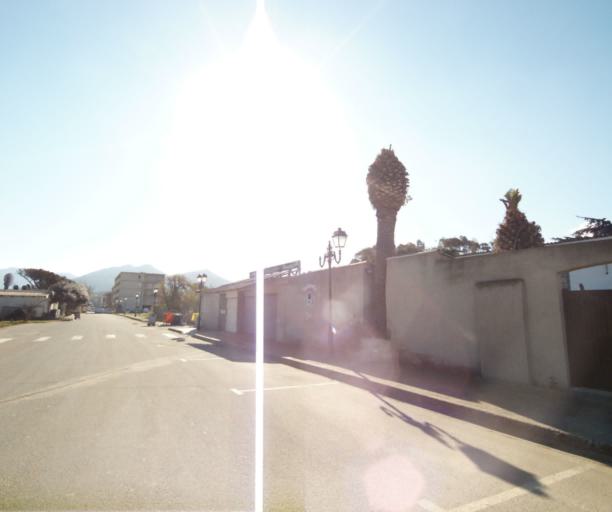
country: FR
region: Corsica
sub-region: Departement de la Corse-du-Sud
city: Propriano
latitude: 41.6748
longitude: 8.8949
